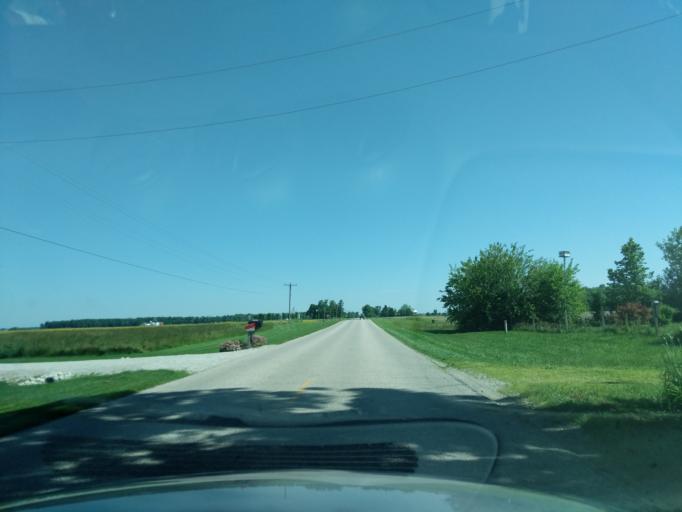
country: US
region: Indiana
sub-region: Huntington County
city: Huntington
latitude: 40.7869
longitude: -85.5077
